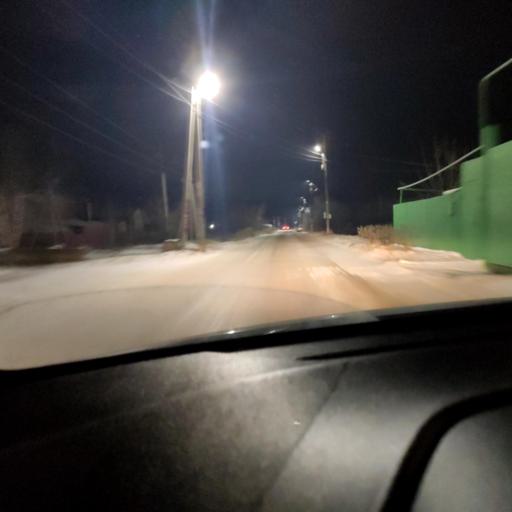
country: RU
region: Tatarstan
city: Staroye Arakchino
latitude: 55.8829
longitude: 49.0401
